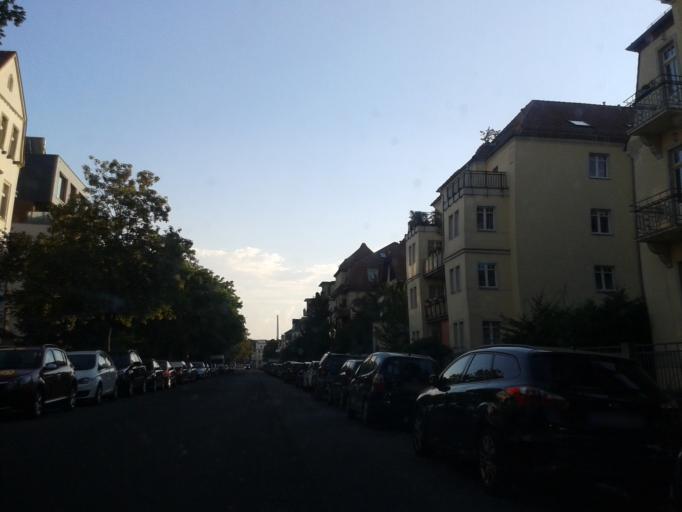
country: DE
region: Saxony
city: Albertstadt
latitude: 51.0443
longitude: 13.8053
